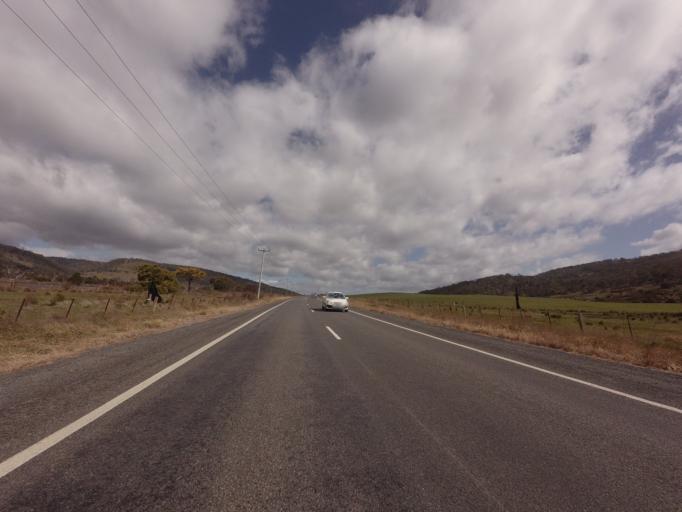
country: AU
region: Tasmania
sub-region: Northern Midlands
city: Evandale
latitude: -41.8115
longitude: 147.5895
